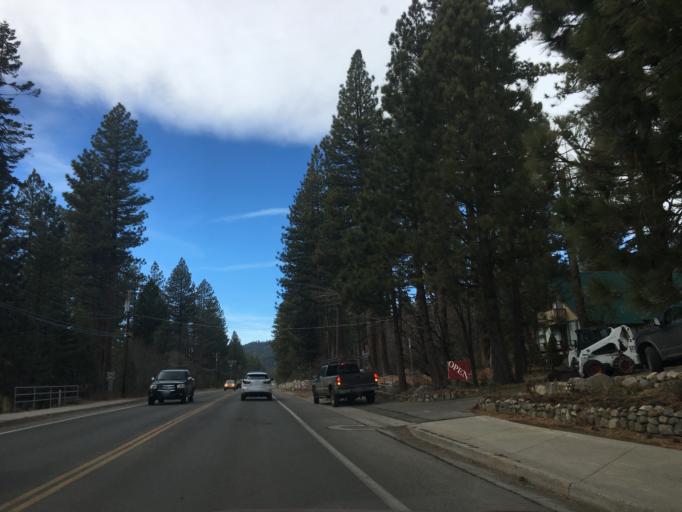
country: US
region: Nevada
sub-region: Washoe County
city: Incline Village
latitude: 39.2499
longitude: -119.9556
